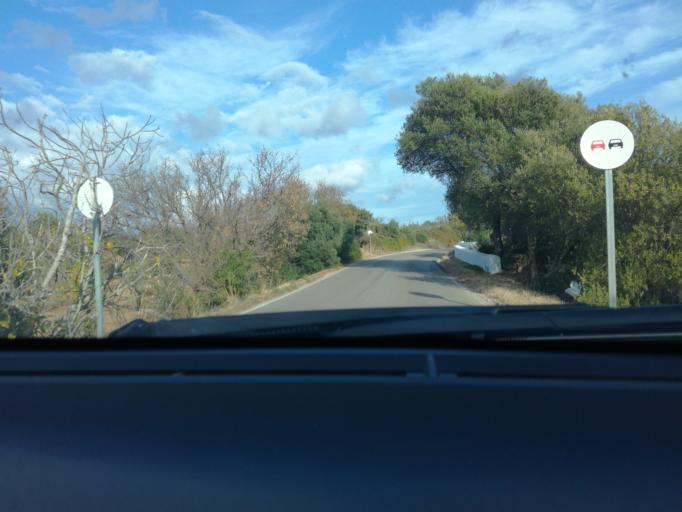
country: PT
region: Faro
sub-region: Olhao
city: Laranjeiro
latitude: 37.0815
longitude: -7.8043
